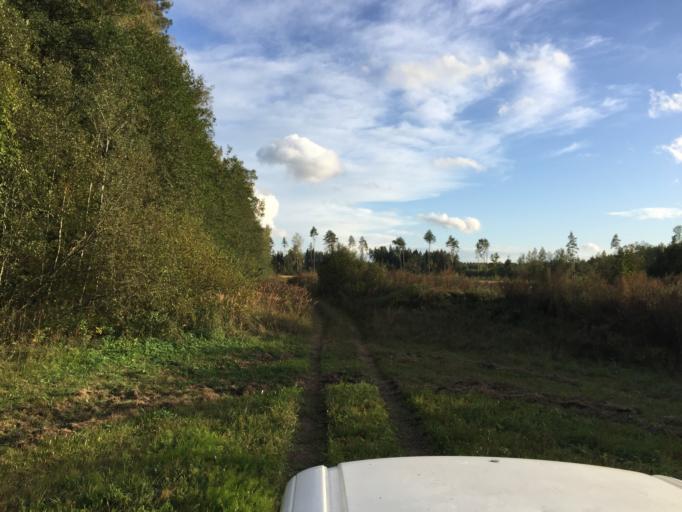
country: LV
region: Malpils
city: Malpils
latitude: 56.9319
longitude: 24.9452
